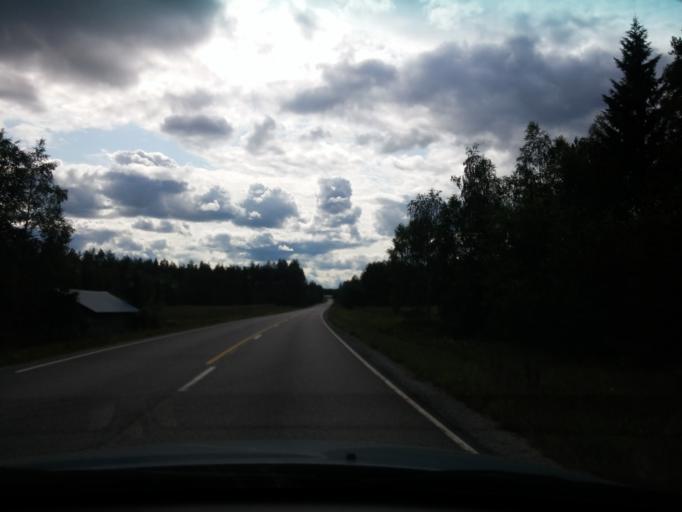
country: FI
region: Central Finland
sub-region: Saarijaervi-Viitasaari
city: Pylkoenmaeki
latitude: 62.6304
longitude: 24.7992
